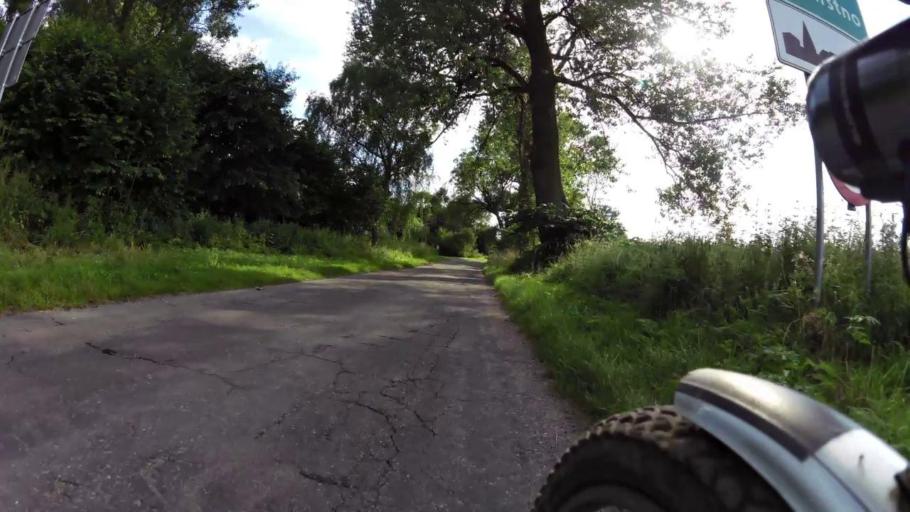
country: PL
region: West Pomeranian Voivodeship
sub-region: Powiat lobeski
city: Wegorzyno
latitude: 53.5419
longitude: 15.4625
